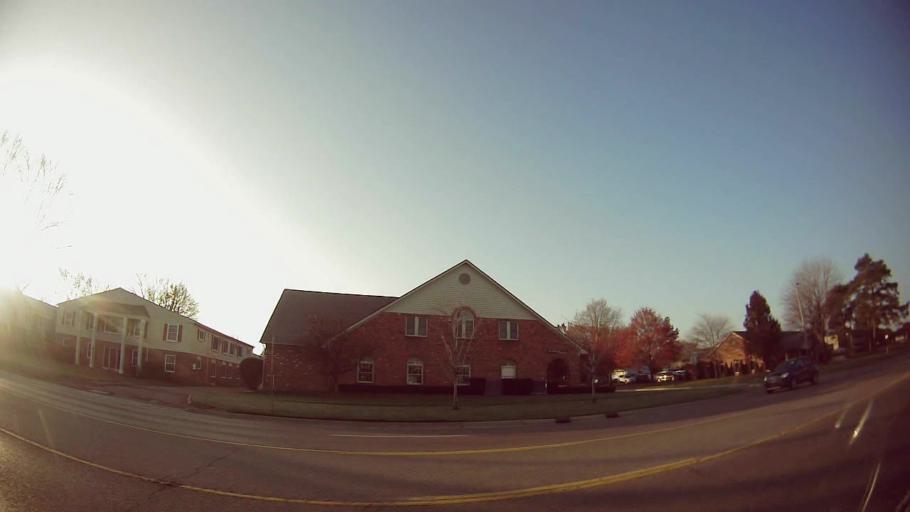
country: US
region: Michigan
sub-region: Oakland County
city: Clawson
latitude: 42.5482
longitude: -83.1578
